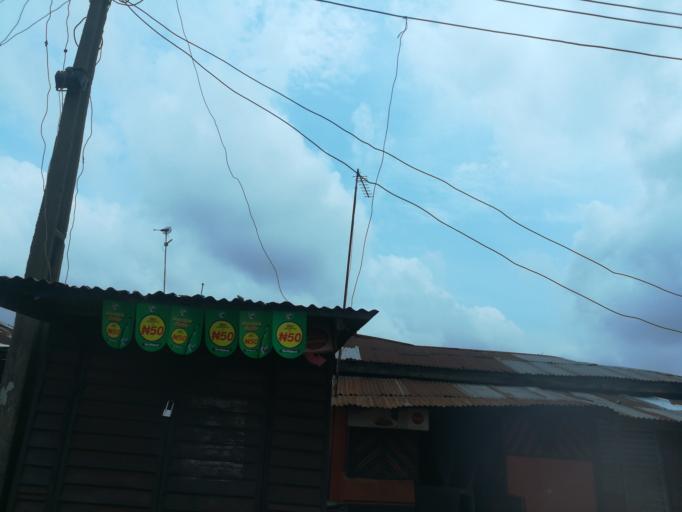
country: NG
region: Lagos
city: Ojota
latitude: 6.5701
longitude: 3.3644
